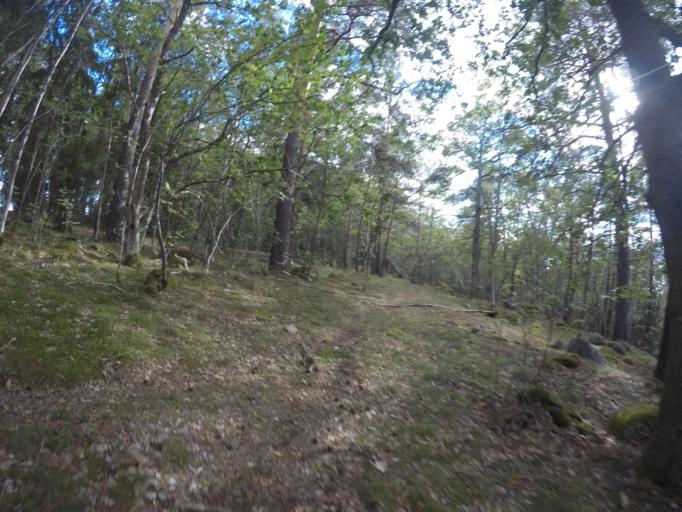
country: SE
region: Soedermanland
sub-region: Eskilstuna Kommun
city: Kvicksund
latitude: 59.4897
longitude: 16.2814
